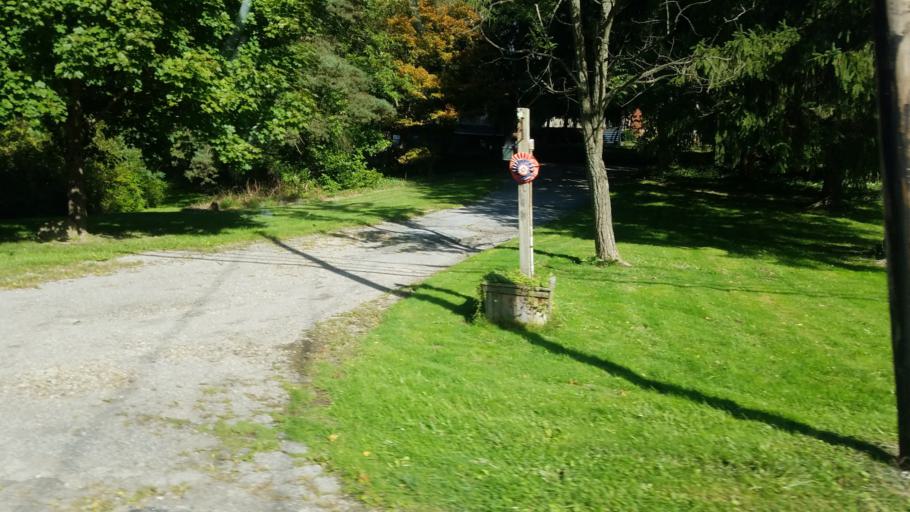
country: US
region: Ohio
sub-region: Trumbull County
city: Mineral Ridge
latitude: 41.1551
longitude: -80.7688
